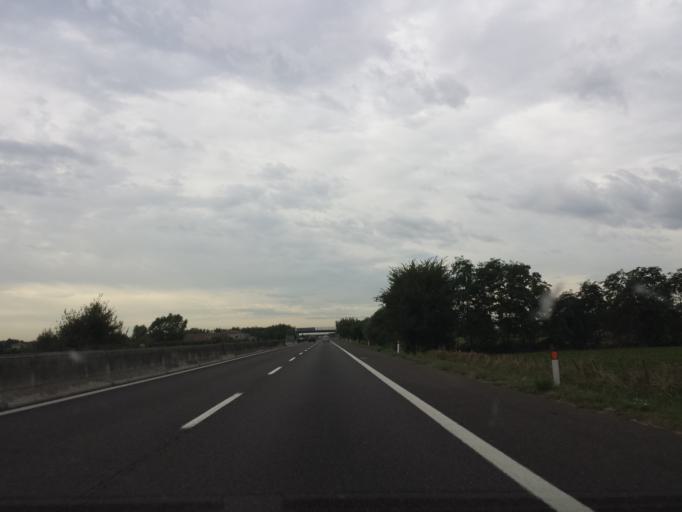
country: IT
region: Veneto
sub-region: Provincia di Padova
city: Monselice
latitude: 45.2250
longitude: 11.7746
